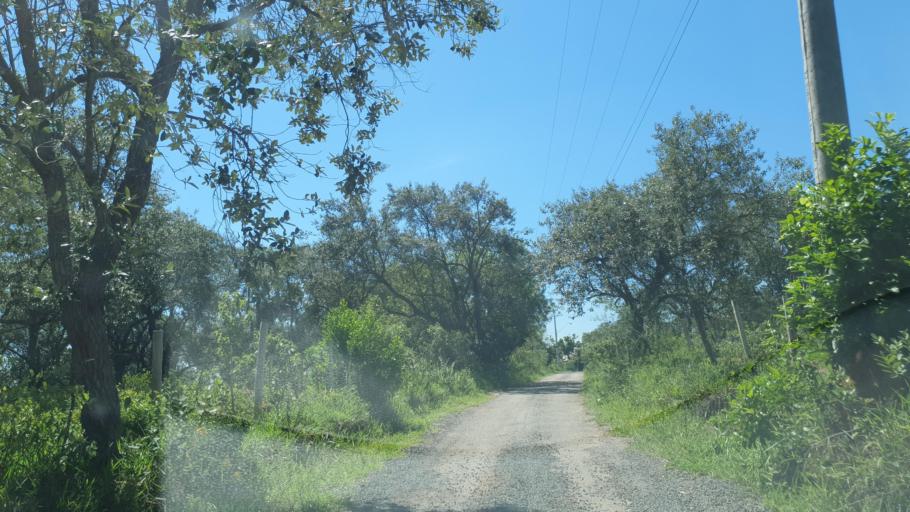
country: BR
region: Sao Paulo
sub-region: Sorocaba
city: Sorocaba
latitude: -23.4132
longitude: -47.4758
